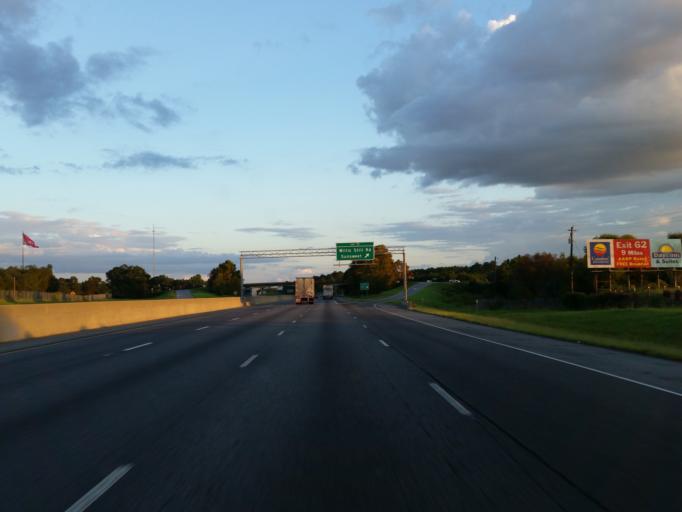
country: US
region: Georgia
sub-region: Tift County
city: Tifton
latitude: 31.5733
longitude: -83.5490
